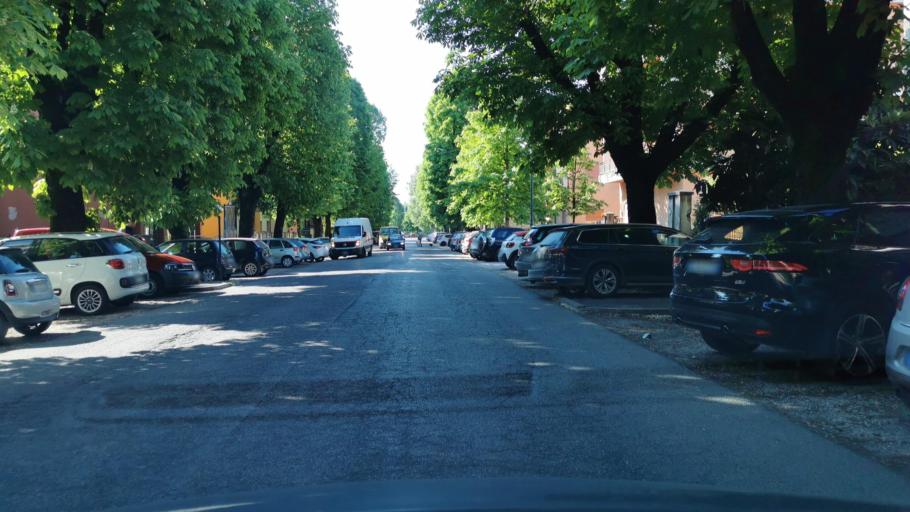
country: IT
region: Lombardy
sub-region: Provincia di Cremona
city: Cremona
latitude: 45.1337
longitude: 10.0375
